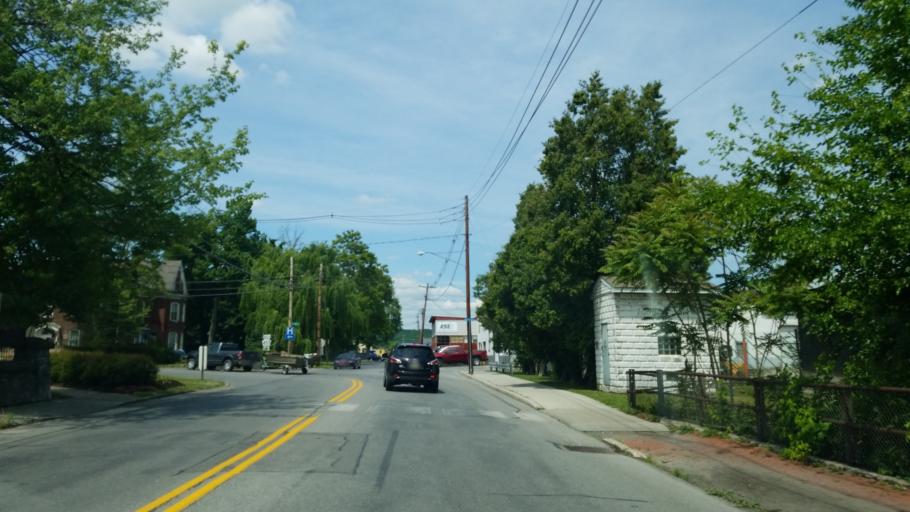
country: US
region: Pennsylvania
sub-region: Blair County
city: Tyrone
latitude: 40.6772
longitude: -78.2393
